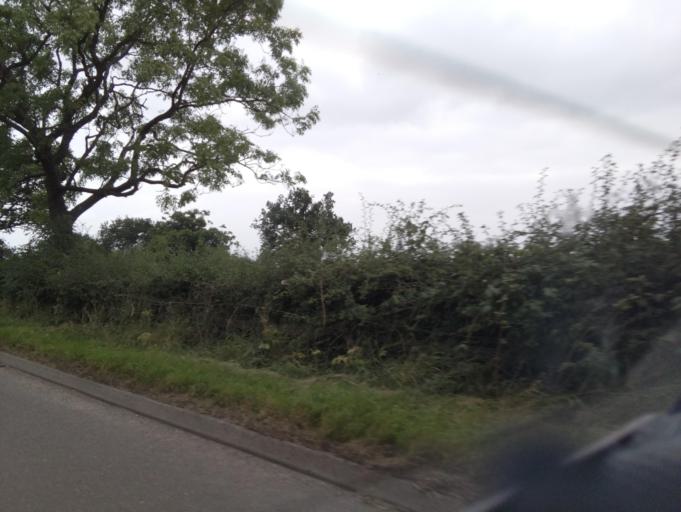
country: GB
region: England
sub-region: Staffordshire
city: Cheadle
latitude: 53.0159
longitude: -2.0223
